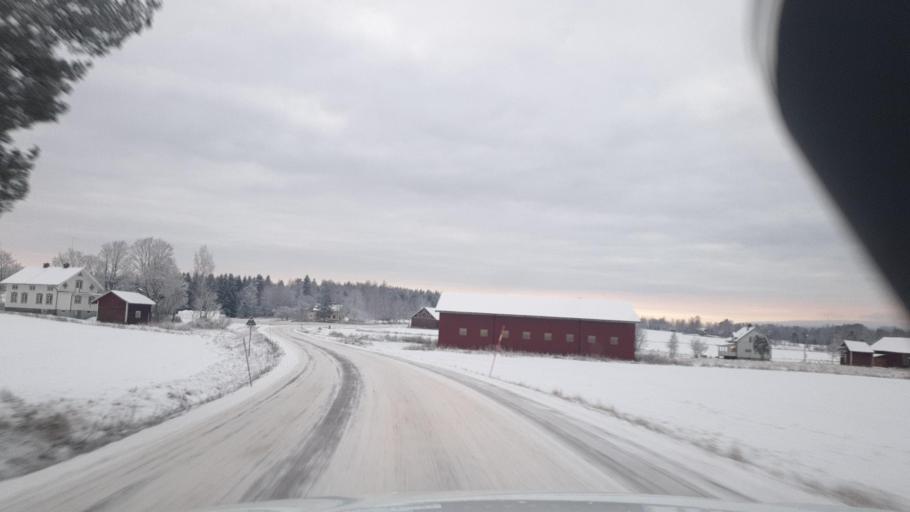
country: SE
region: Vaermland
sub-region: Eda Kommun
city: Charlottenberg
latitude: 59.7689
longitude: 12.1608
